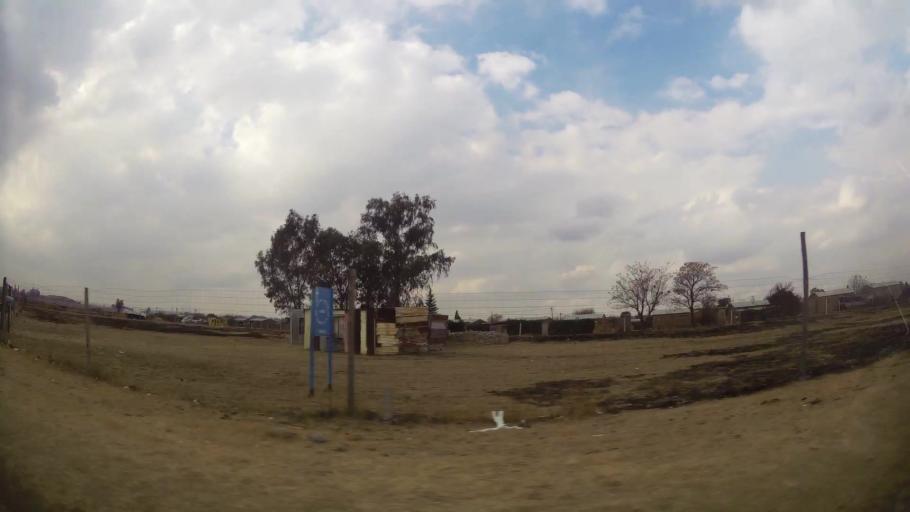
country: ZA
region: Orange Free State
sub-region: Fezile Dabi District Municipality
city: Sasolburg
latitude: -26.8486
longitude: 27.8751
